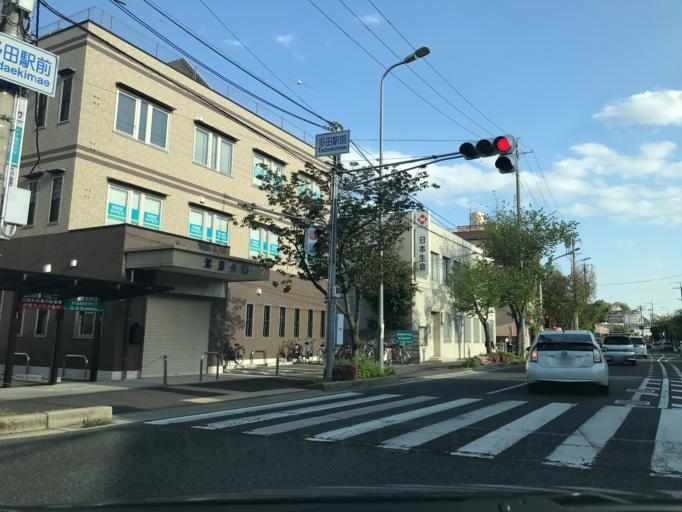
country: JP
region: Osaka
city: Ikeda
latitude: 34.8609
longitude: 135.4156
